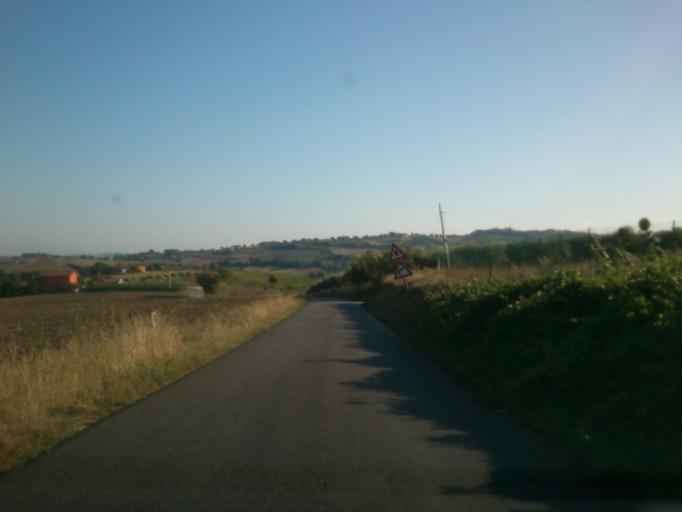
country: IT
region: The Marches
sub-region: Provincia di Pesaro e Urbino
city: Lucrezia
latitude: 43.7879
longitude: 12.9103
